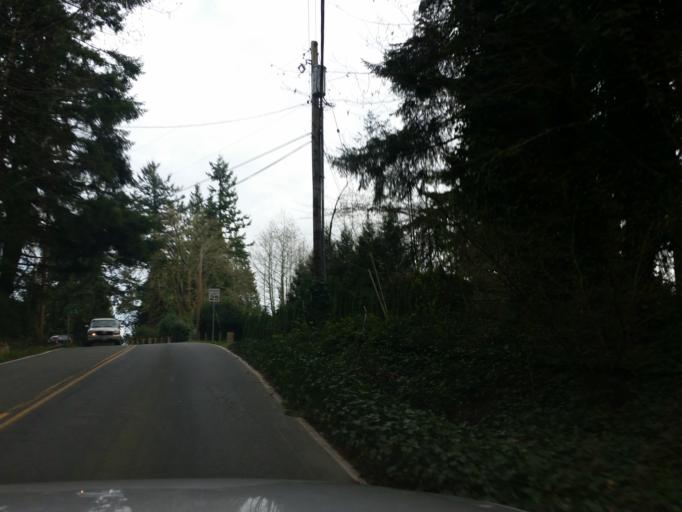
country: US
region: Washington
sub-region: King County
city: Woodinville
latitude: 47.7548
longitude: -122.1316
